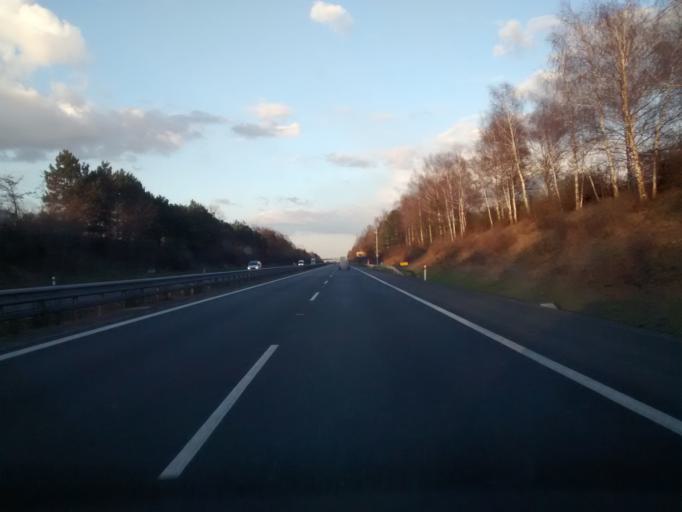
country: CZ
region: Central Bohemia
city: Nehvizdy
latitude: 50.1273
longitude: 14.7379
